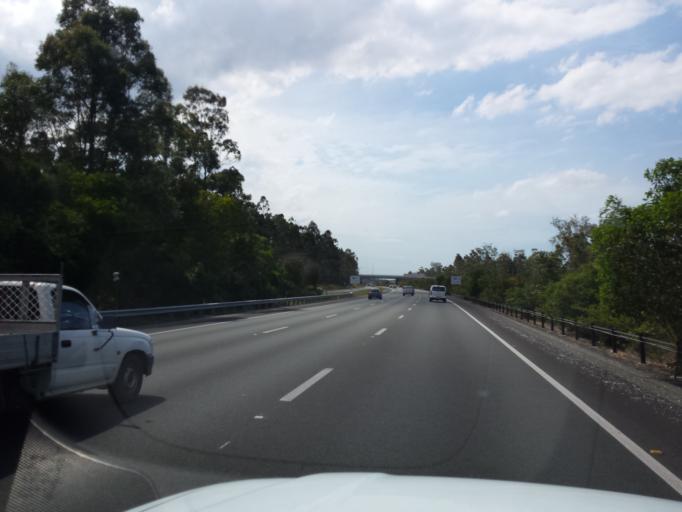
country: AU
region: Queensland
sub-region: Gold Coast
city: Nerang
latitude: -27.9555
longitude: 153.3441
